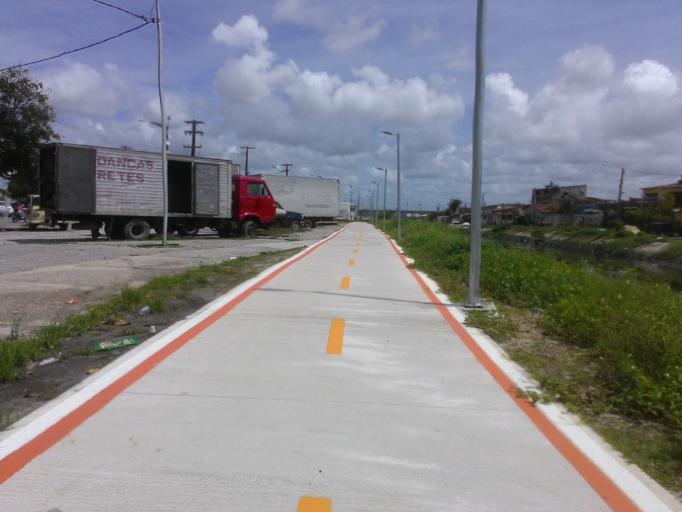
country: BR
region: Pernambuco
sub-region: Olinda
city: Olinda
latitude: -8.0198
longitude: -34.8555
